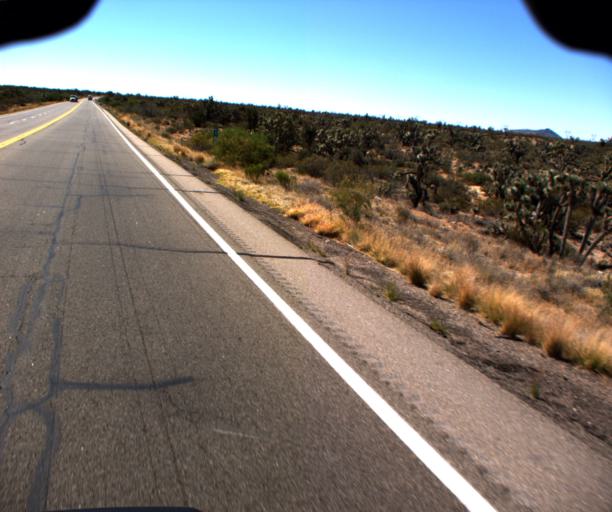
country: US
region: Arizona
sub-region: Yavapai County
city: Congress
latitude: 34.2753
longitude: -113.0982
